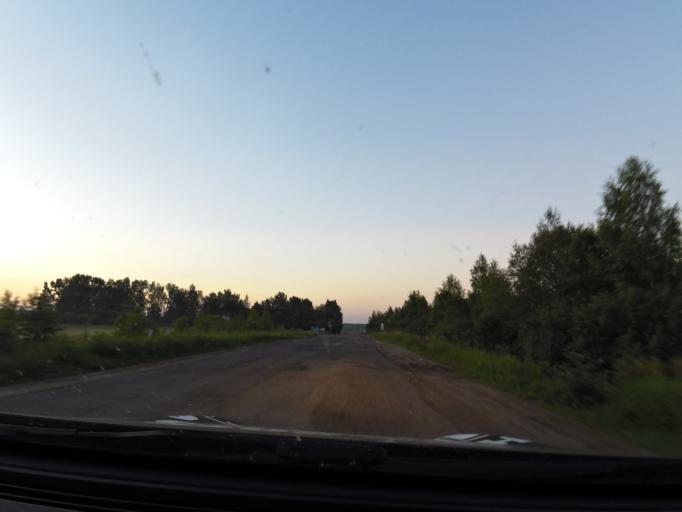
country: RU
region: Kostroma
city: Buy
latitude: 58.4770
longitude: 41.4366
